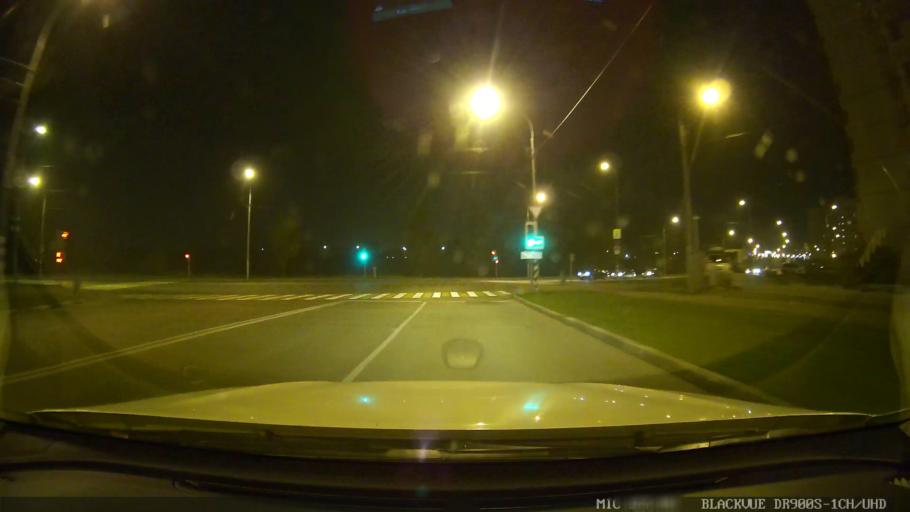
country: RU
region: Moskovskaya
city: Shcherbinka
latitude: 55.5020
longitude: 37.5814
